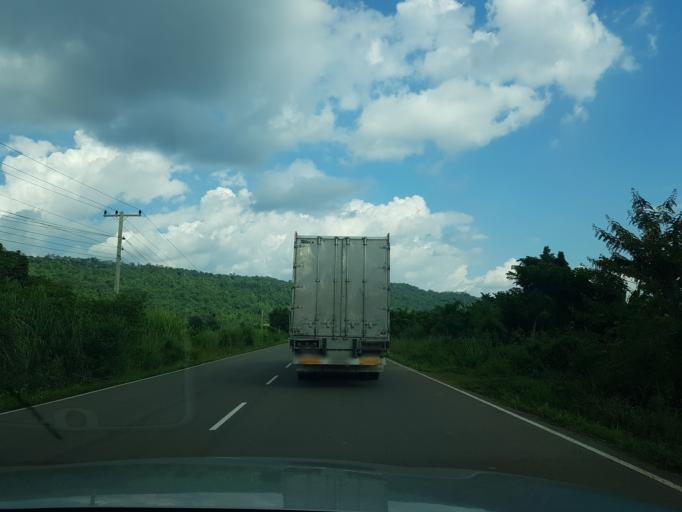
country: TH
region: Nong Khai
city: Sangkhom
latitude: 18.0243
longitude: 102.3843
